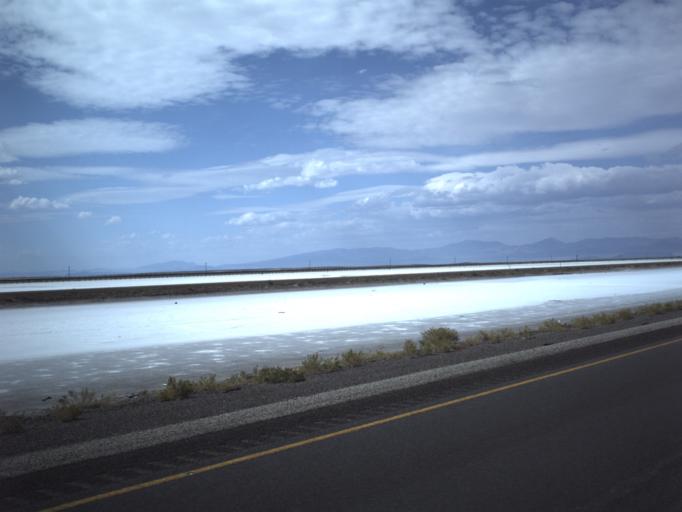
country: US
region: Utah
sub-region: Tooele County
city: Wendover
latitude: 40.7364
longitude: -113.7079
